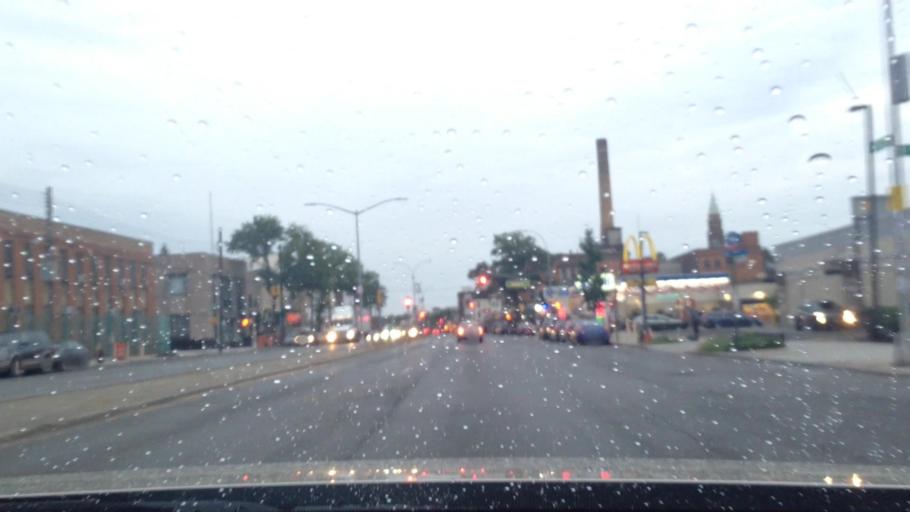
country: US
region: New York
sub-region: Kings County
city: East New York
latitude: 40.6764
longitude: -73.8914
